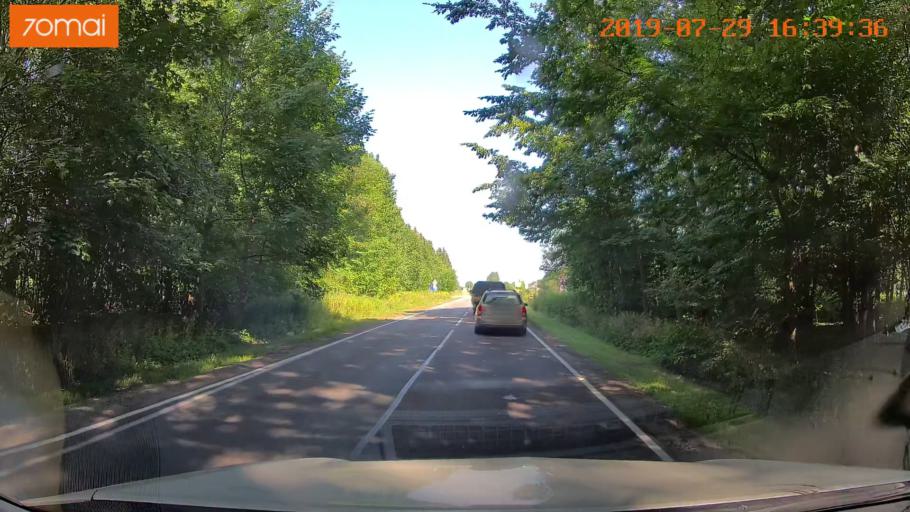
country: RU
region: Kaliningrad
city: Primorsk
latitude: 54.7403
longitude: 20.0639
